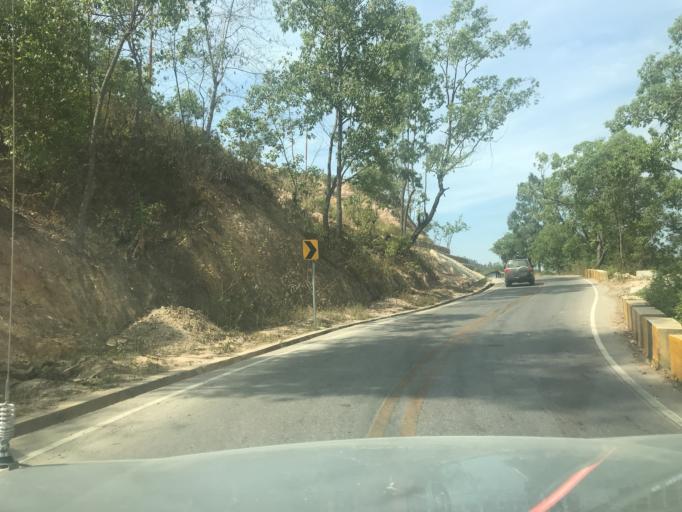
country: TL
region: Aileu
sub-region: Aileu Villa
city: Aileu
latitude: -8.6815
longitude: 125.5513
